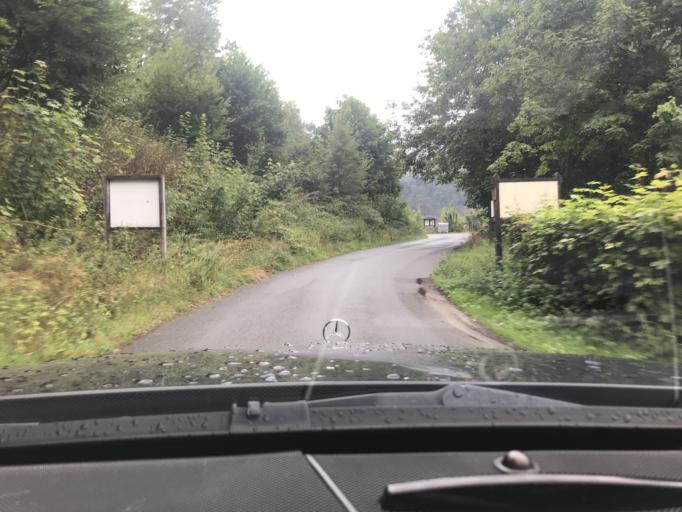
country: DE
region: Lower Saxony
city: Bad Lauterberg im Harz
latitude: 51.6457
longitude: 10.5130
